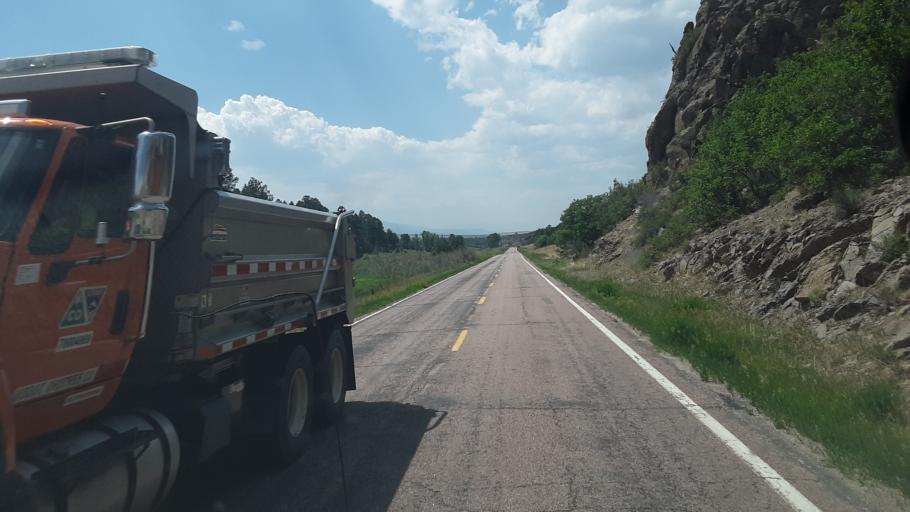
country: US
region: Colorado
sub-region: Custer County
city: Westcliffe
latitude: 38.2537
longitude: -105.5851
